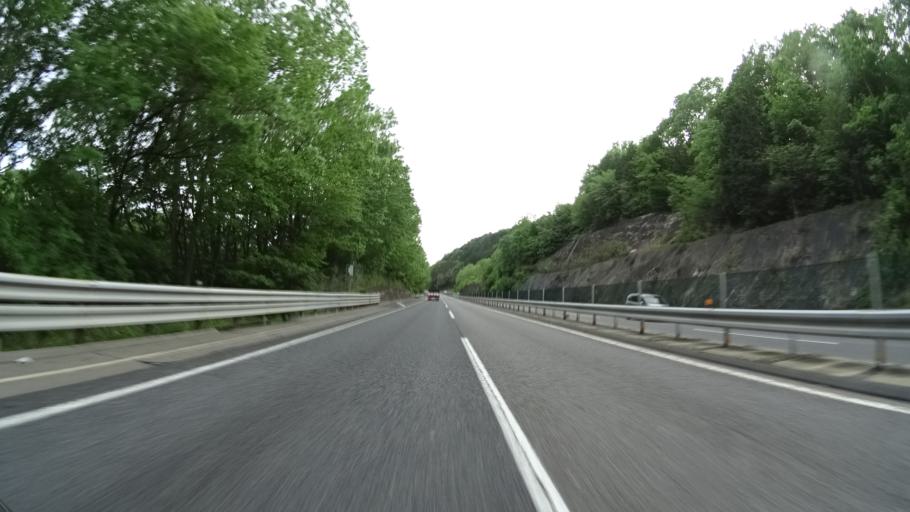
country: JP
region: Gifu
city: Mizunami
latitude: 35.4304
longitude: 137.3327
